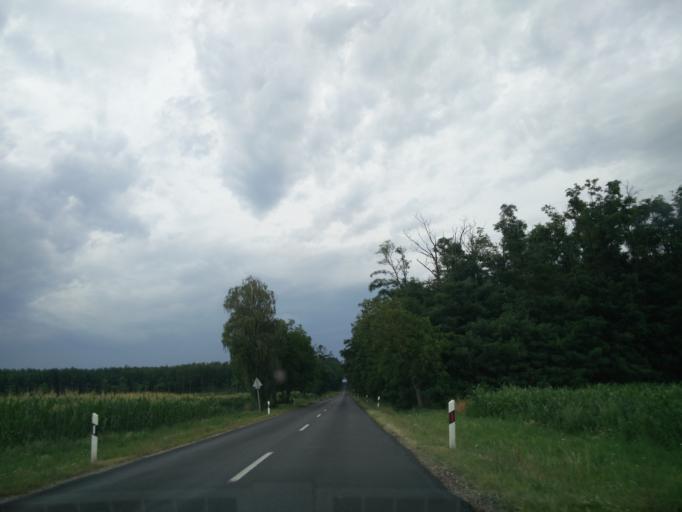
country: HU
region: Vas
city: Vasvar
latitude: 47.0197
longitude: 16.8210
